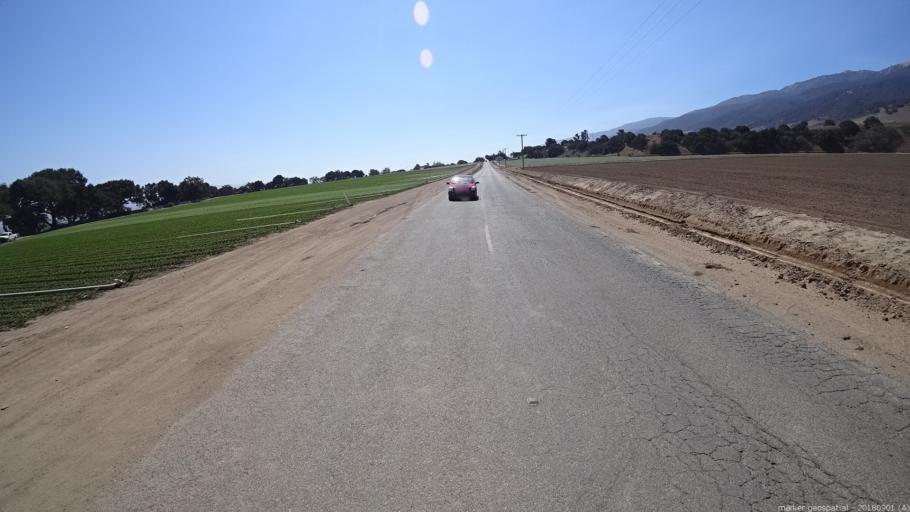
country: US
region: California
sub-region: Monterey County
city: Chualar
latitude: 36.5273
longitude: -121.5266
